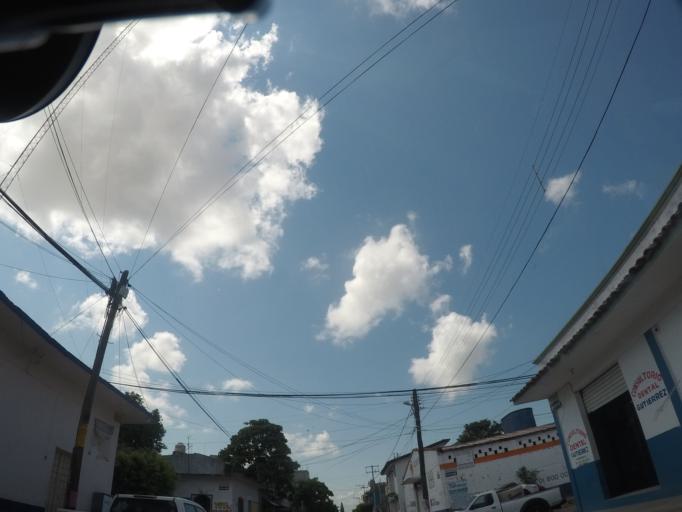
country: MX
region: Oaxaca
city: Juchitan de Zaragoza
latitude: 16.4369
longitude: -95.0200
